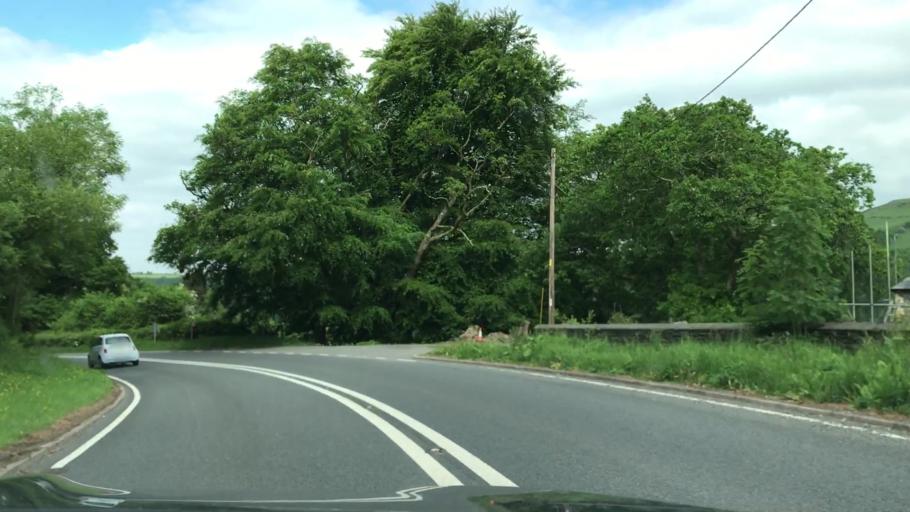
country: GB
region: Wales
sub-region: County of Ceredigion
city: Bow Street
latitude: 52.4123
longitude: -3.9229
